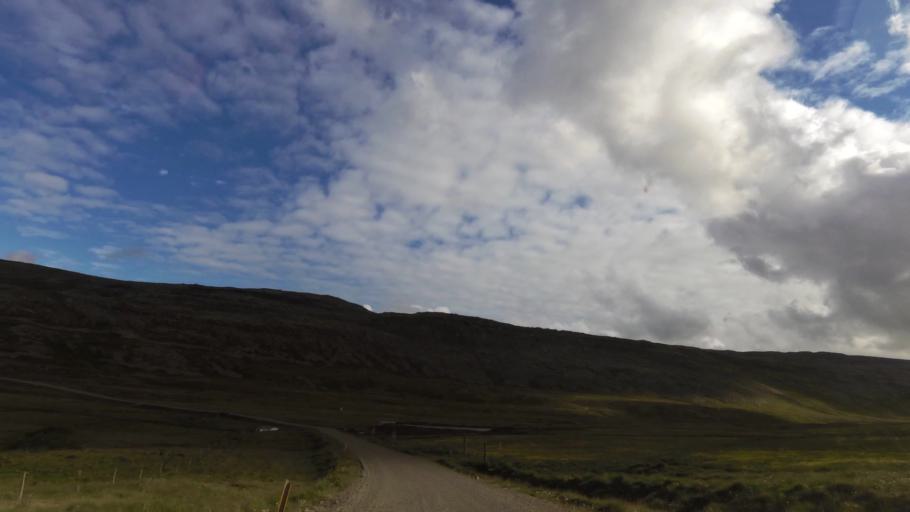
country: IS
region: West
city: Olafsvik
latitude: 65.5614
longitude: -24.1781
